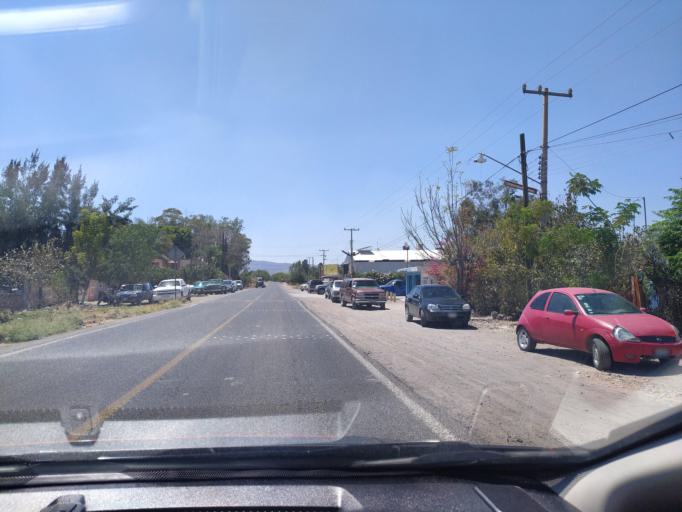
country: MX
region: Guanajuato
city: Ciudad Manuel Doblado
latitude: 20.7442
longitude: -101.9030
